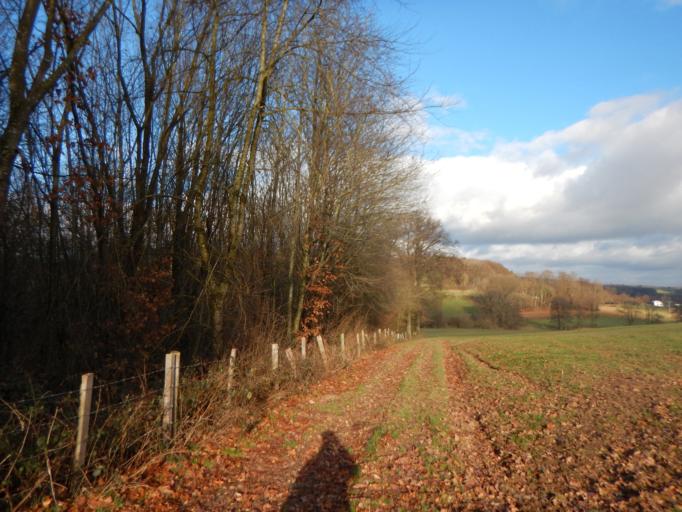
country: LU
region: Diekirch
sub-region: Canton de Redange
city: Redange-sur-Attert
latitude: 49.7672
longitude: 5.9125
